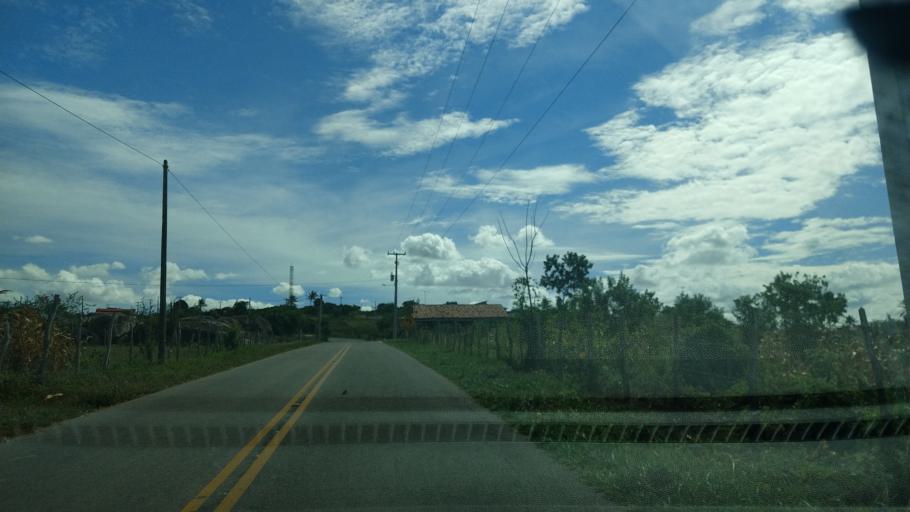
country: BR
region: Rio Grande do Norte
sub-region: Sao Jose Do Campestre
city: Sao Jose do Campestre
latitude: -6.4187
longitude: -35.7263
